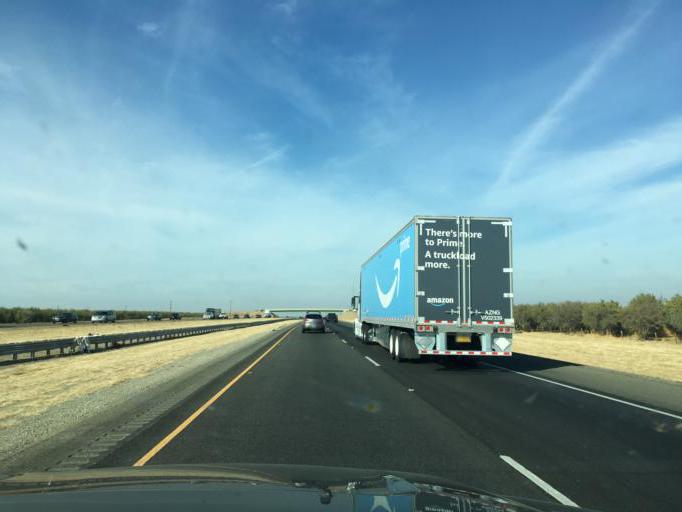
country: US
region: California
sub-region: Merced County
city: South Dos Palos
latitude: 36.7164
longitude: -120.6817
